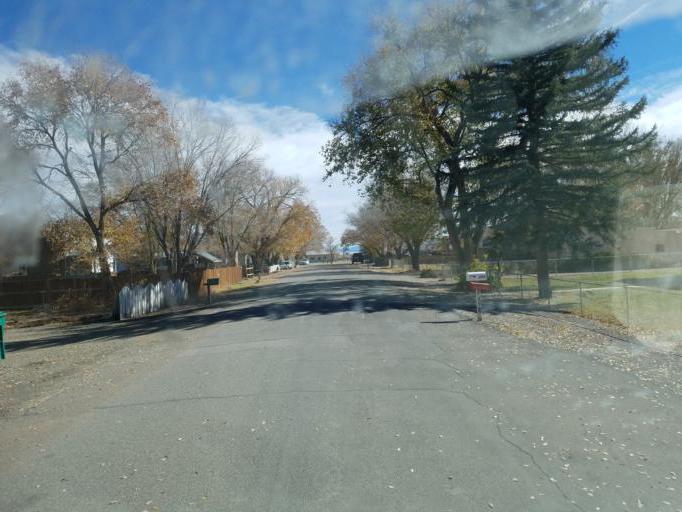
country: US
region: Colorado
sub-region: Alamosa County
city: Alamosa East
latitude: 37.4816
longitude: -105.8532
